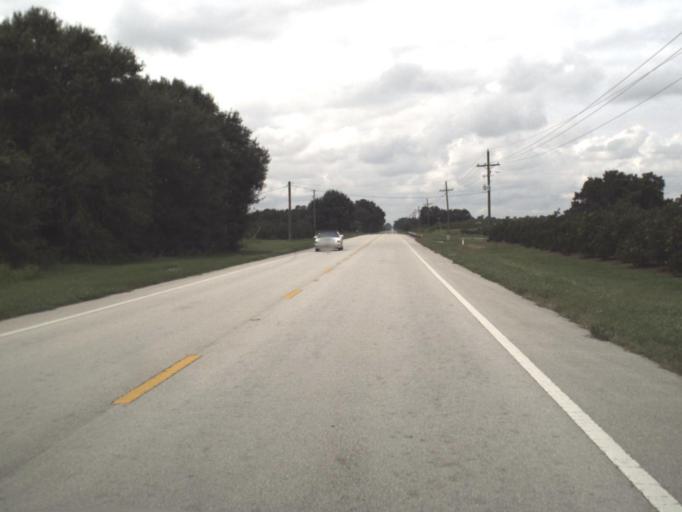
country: US
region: Florida
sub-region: Hardee County
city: Bowling Green
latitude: 27.5948
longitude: -81.8984
